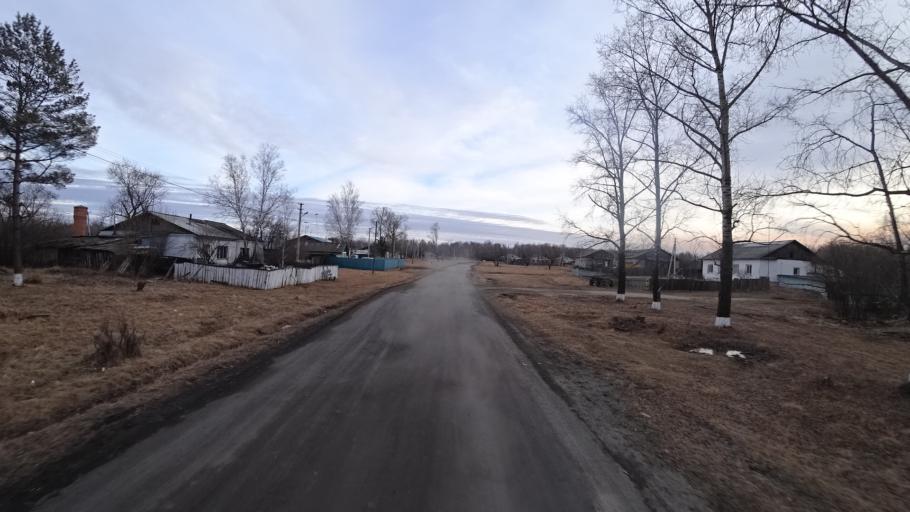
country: RU
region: Amur
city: Bureya
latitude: 50.0178
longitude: 129.7682
